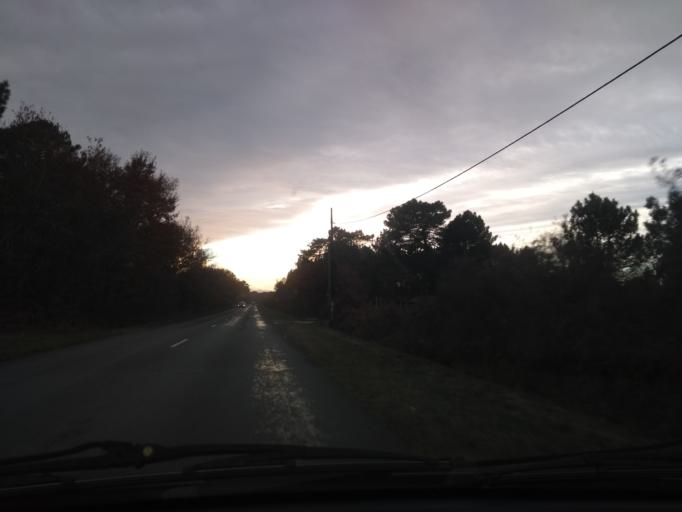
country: FR
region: Aquitaine
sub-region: Departement de la Gironde
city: Saucats
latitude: 44.6395
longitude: -0.6403
